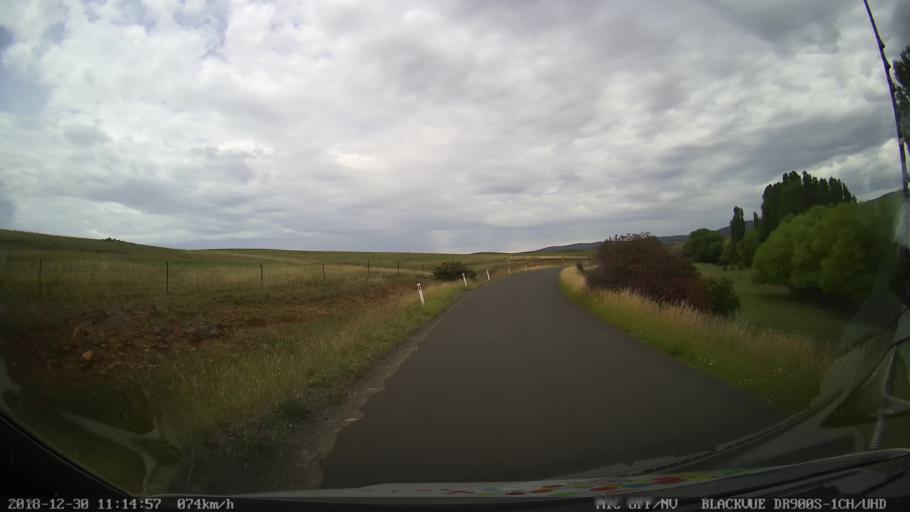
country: AU
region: New South Wales
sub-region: Snowy River
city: Jindabyne
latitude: -36.5411
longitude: 148.7273
